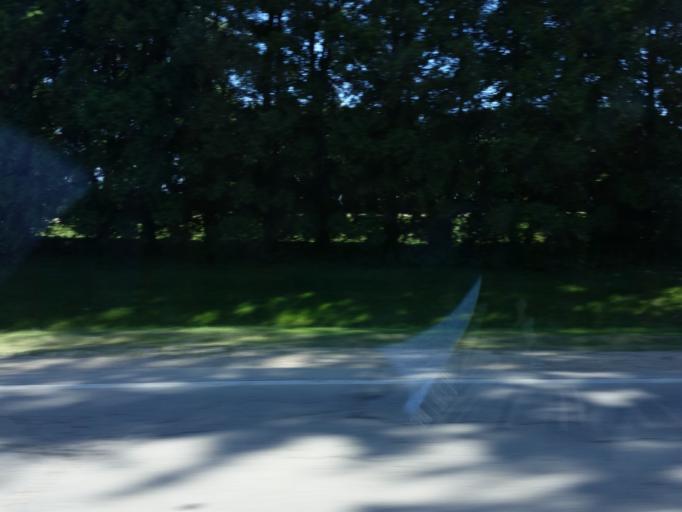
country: US
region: Illinois
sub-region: Ogle County
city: Davis Junction
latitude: 42.1003
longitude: -89.0588
